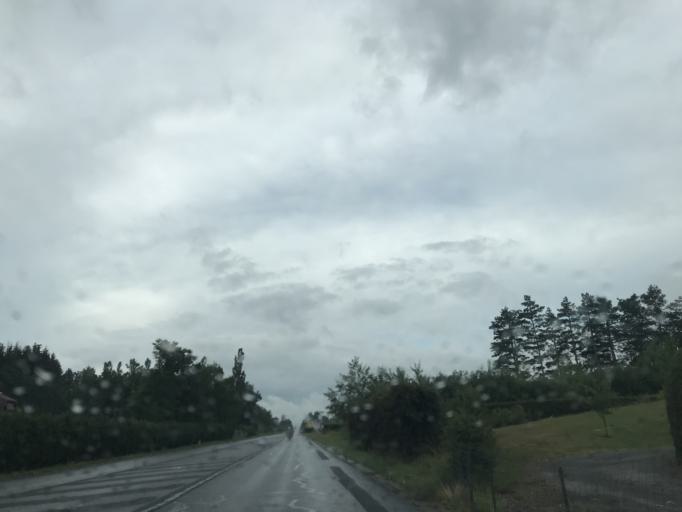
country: FR
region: Auvergne
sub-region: Departement du Puy-de-Dome
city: Ambert
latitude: 45.5282
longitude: 3.7278
